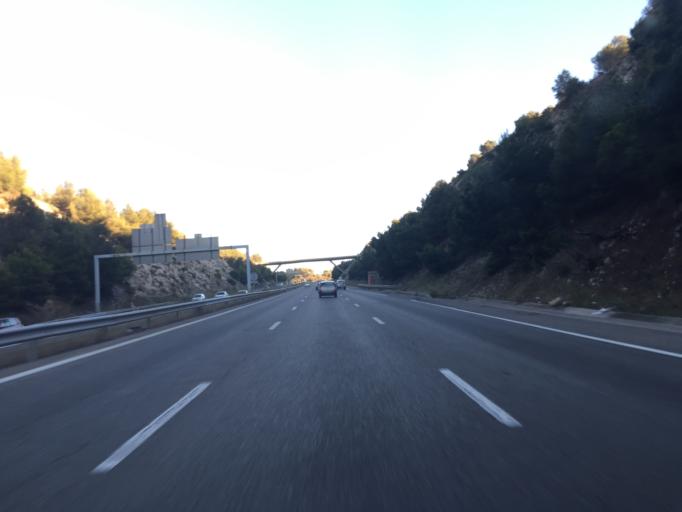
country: FR
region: Provence-Alpes-Cote d'Azur
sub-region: Departement des Bouches-du-Rhone
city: Les Pennes-Mirabeau
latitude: 43.3917
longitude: 5.3010
